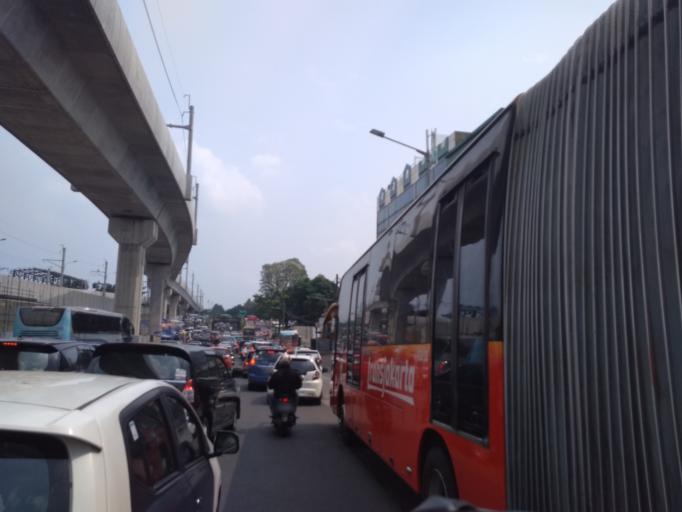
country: ID
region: Banten
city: South Tangerang
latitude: -6.2891
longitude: 106.7728
